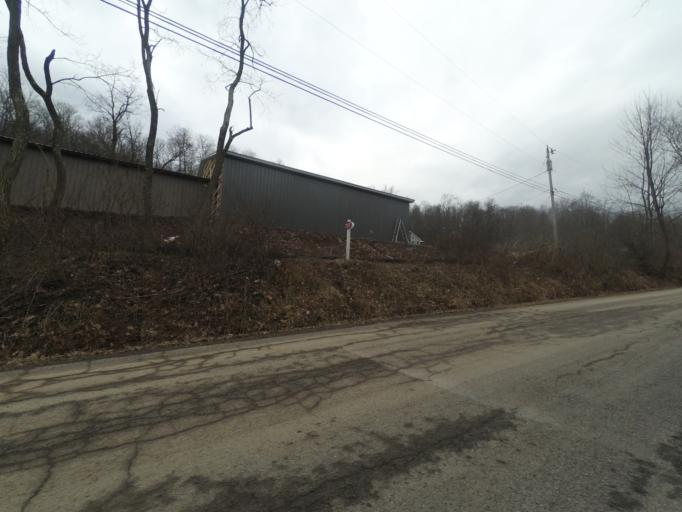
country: US
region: Pennsylvania
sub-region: Centre County
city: Stormstown
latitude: 40.8696
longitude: -78.0090
